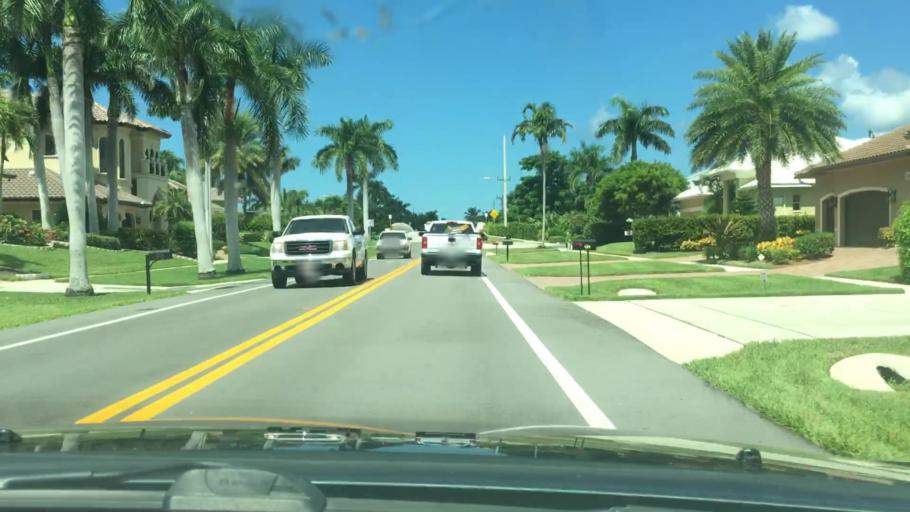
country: US
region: Florida
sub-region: Collier County
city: Marco
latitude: 25.9498
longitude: -81.7366
